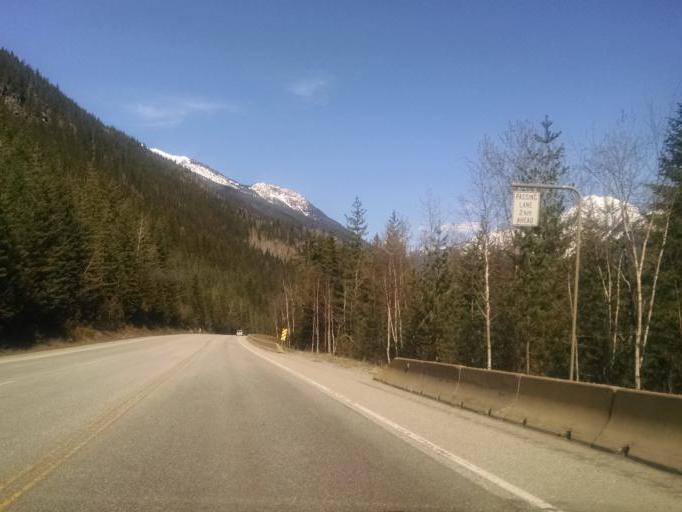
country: CA
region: British Columbia
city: Revelstoke
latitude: 51.0239
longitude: -118.0538
